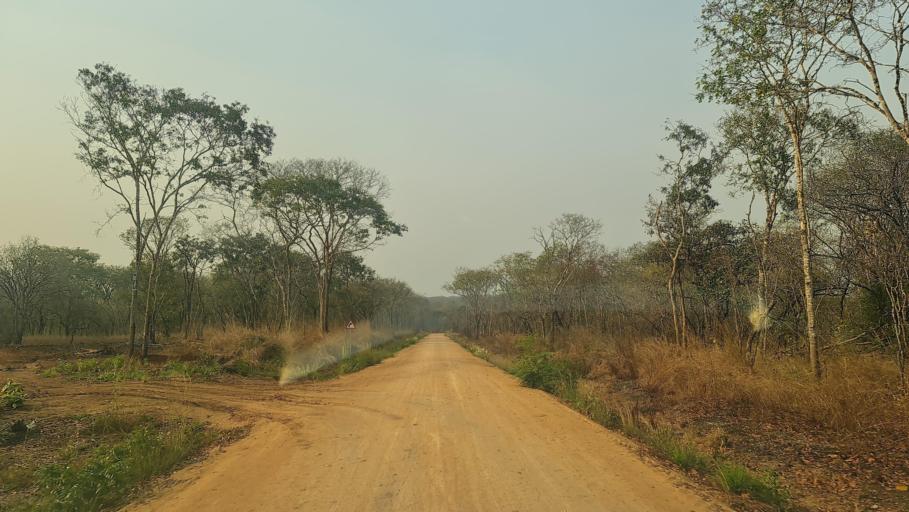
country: MZ
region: Zambezia
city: Quelimane
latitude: -17.1445
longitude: 37.1355
